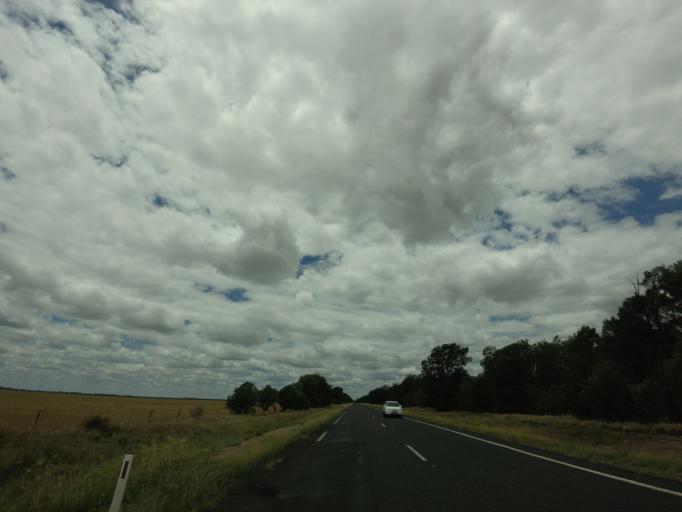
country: AU
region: Queensland
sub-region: Goondiwindi
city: Goondiwindi
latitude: -28.1661
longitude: 150.5478
